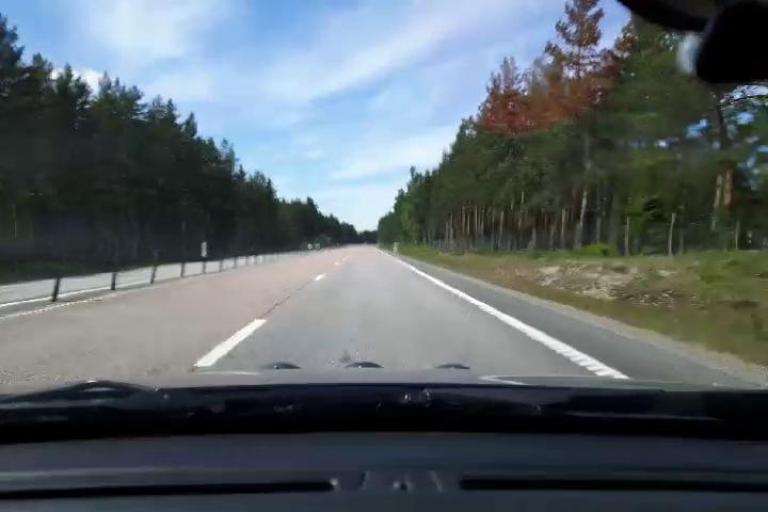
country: SE
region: Gaevleborg
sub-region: Gavle Kommun
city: Norrsundet
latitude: 60.9917
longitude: 17.0032
